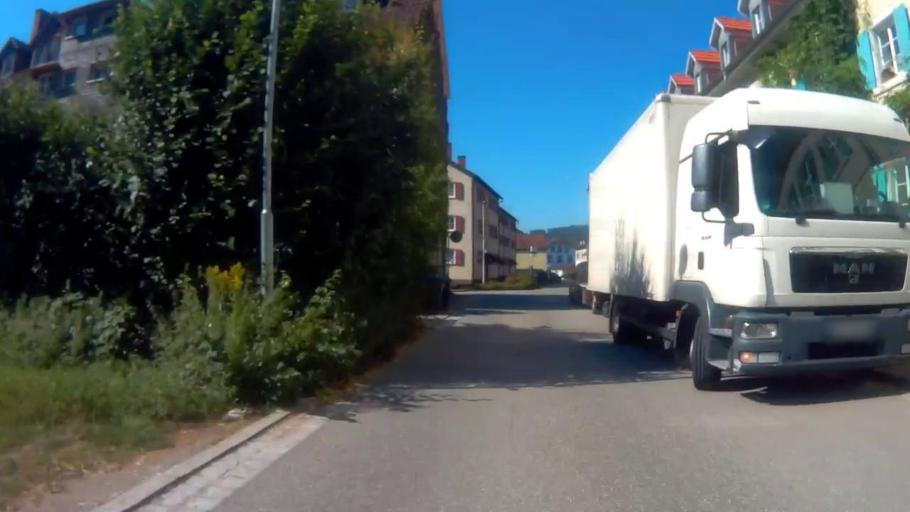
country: DE
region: Baden-Wuerttemberg
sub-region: Freiburg Region
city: Hausen
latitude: 47.6860
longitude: 7.8428
